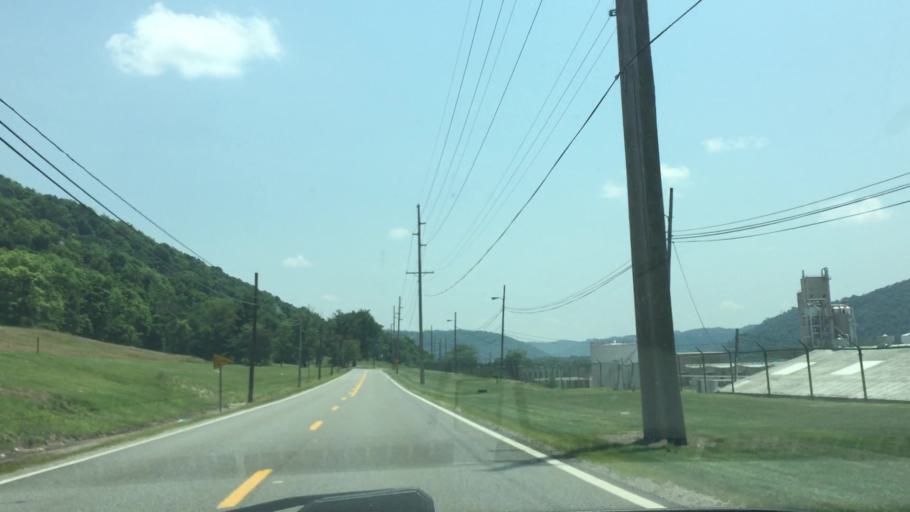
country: US
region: West Virginia
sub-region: Wetzel County
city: New Martinsville
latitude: 39.7450
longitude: -80.8462
